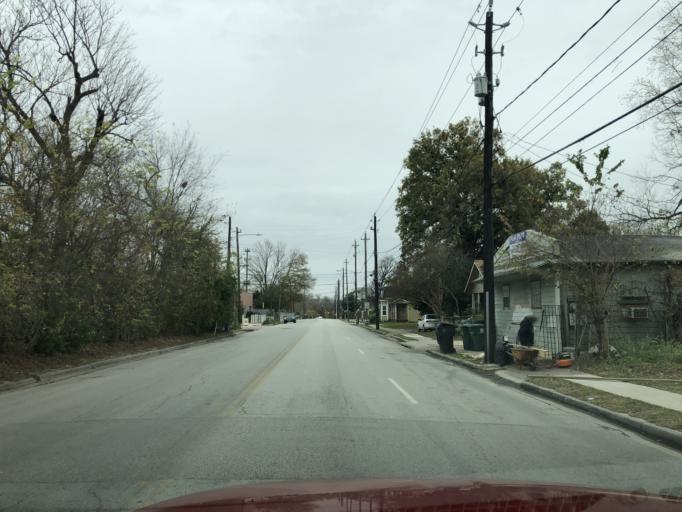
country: US
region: Texas
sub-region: Harris County
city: Houston
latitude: 29.7876
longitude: -95.3689
